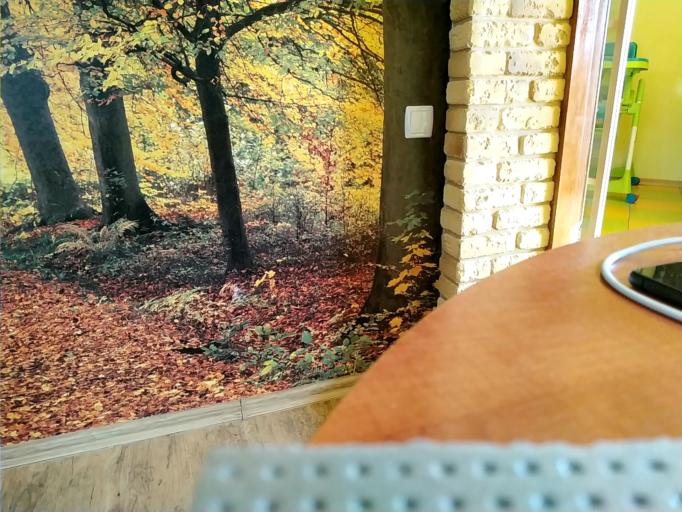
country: RU
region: Tverskaya
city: Kalashnikovo
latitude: 57.3495
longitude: 35.1915
